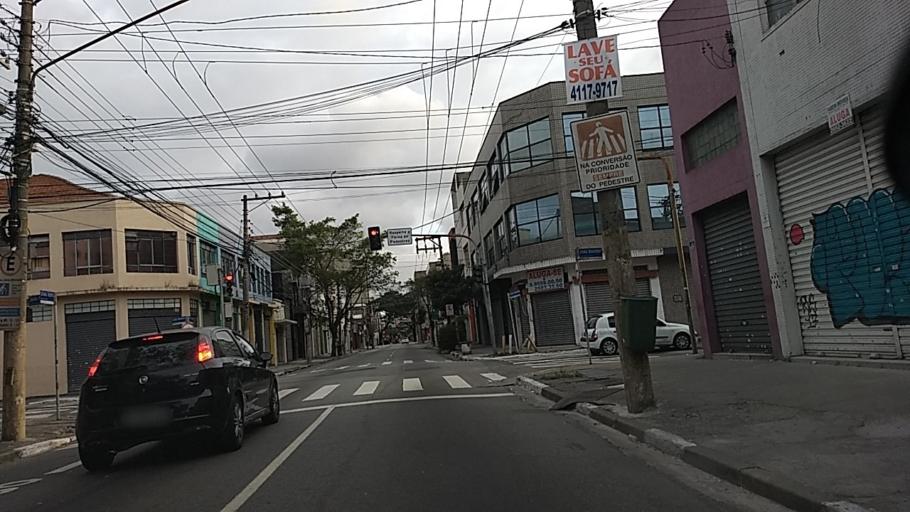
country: BR
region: Sao Paulo
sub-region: Sao Paulo
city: Sao Paulo
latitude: -23.5317
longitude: -46.6122
